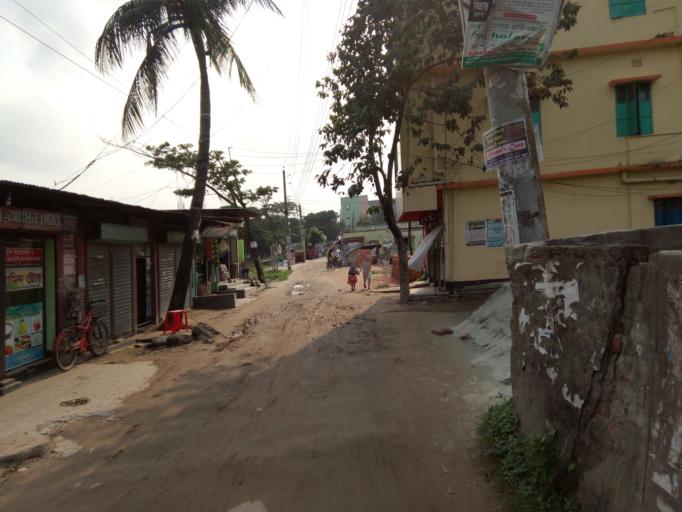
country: BD
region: Dhaka
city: Paltan
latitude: 23.7075
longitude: 90.5000
